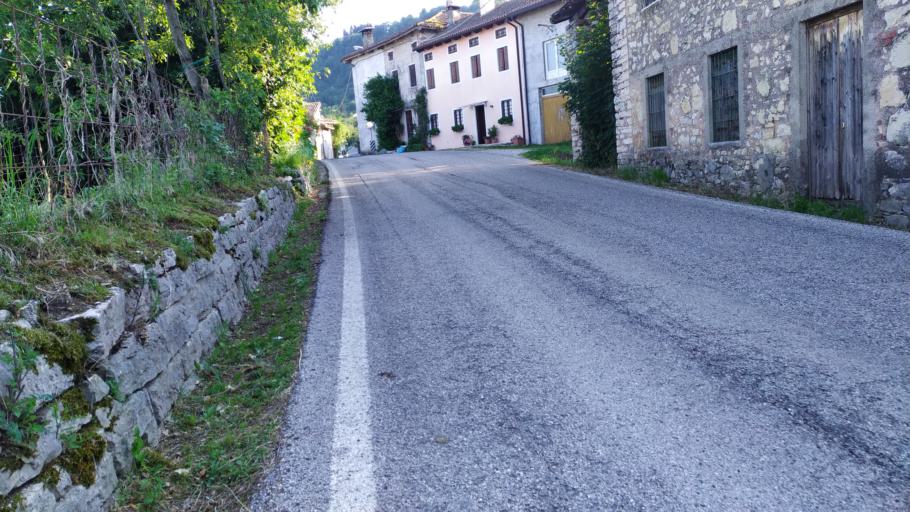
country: IT
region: Veneto
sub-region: Provincia di Vicenza
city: Schio
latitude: 45.6844
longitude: 11.3358
